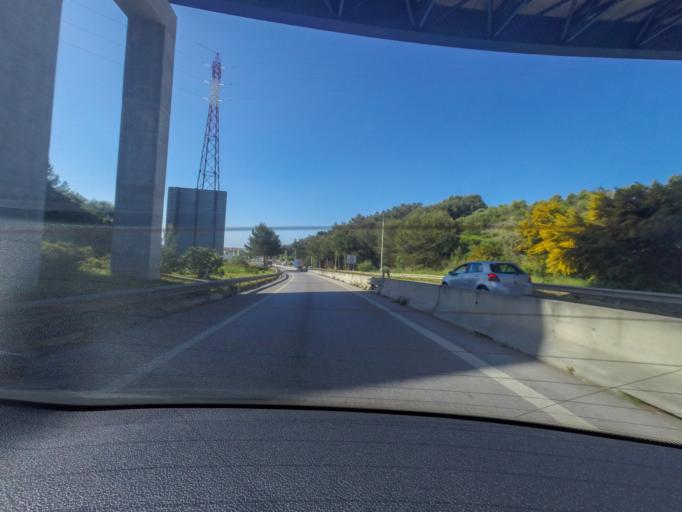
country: PT
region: Lisbon
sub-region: Cascais
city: Alcabideche
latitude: 38.7259
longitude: -9.4172
